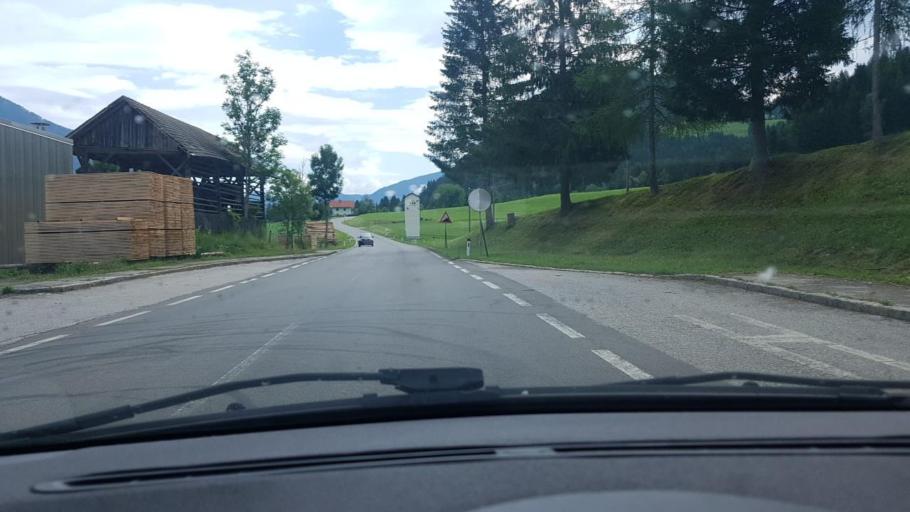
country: AT
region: Carinthia
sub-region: Politischer Bezirk Spittal an der Drau
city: Greifenburg
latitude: 46.7394
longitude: 13.2111
